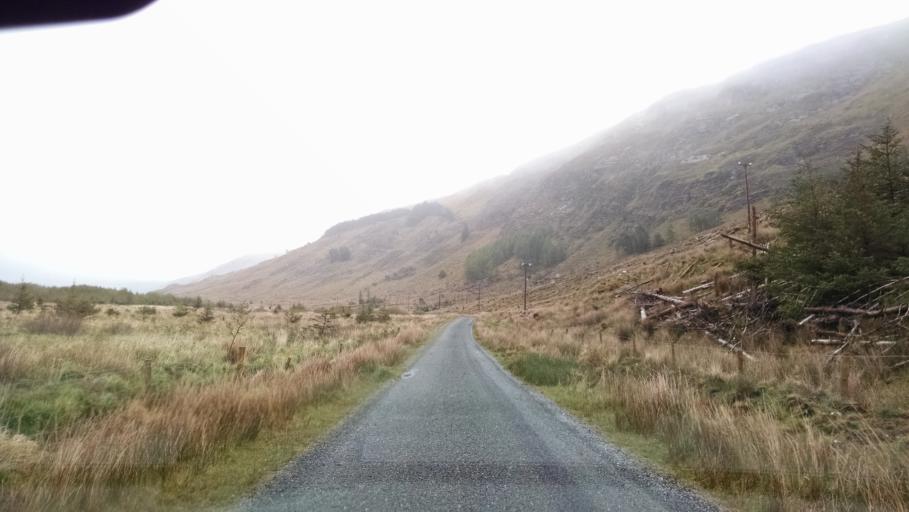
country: IE
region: Connaught
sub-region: Maigh Eo
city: Westport
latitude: 53.6446
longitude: -9.7021
